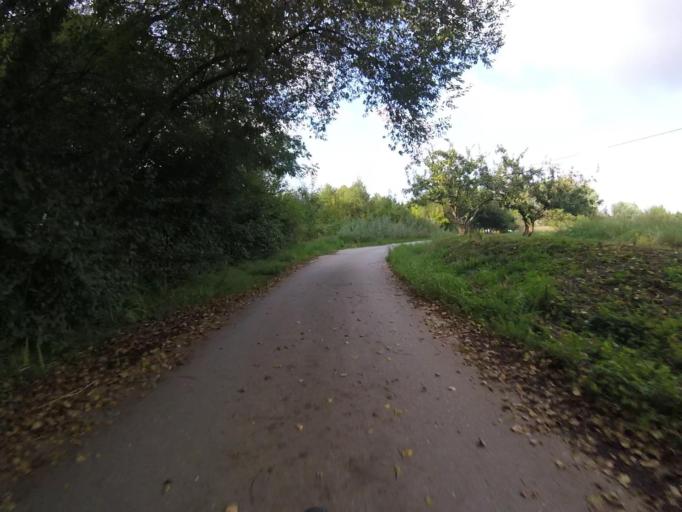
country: ES
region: Basque Country
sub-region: Provincia de Guipuzcoa
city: Irun
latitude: 43.3438
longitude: -1.8204
